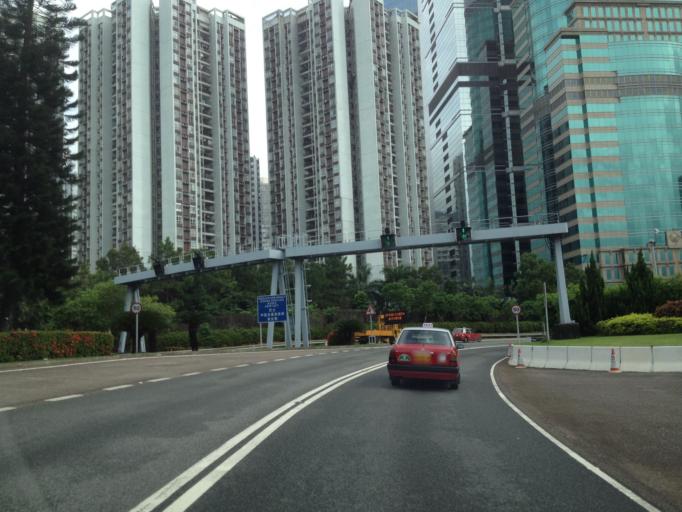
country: HK
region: Kowloon City
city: Kowloon
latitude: 22.2892
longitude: 114.2143
